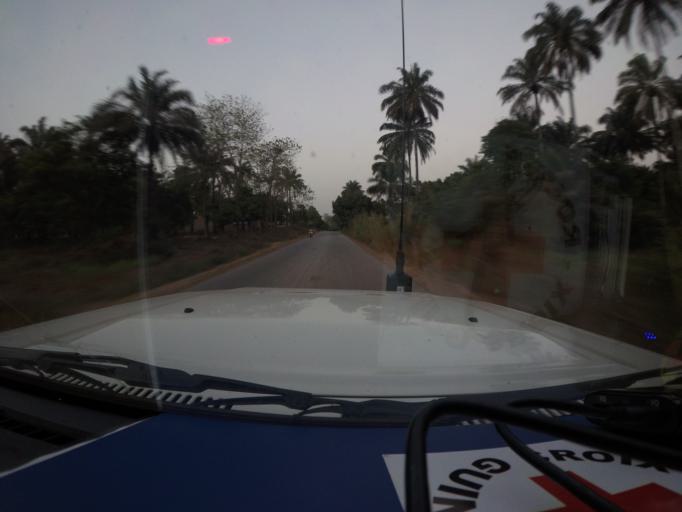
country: GN
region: Kindia
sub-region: Kindia
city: Kindia
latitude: 9.9409
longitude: -12.9730
